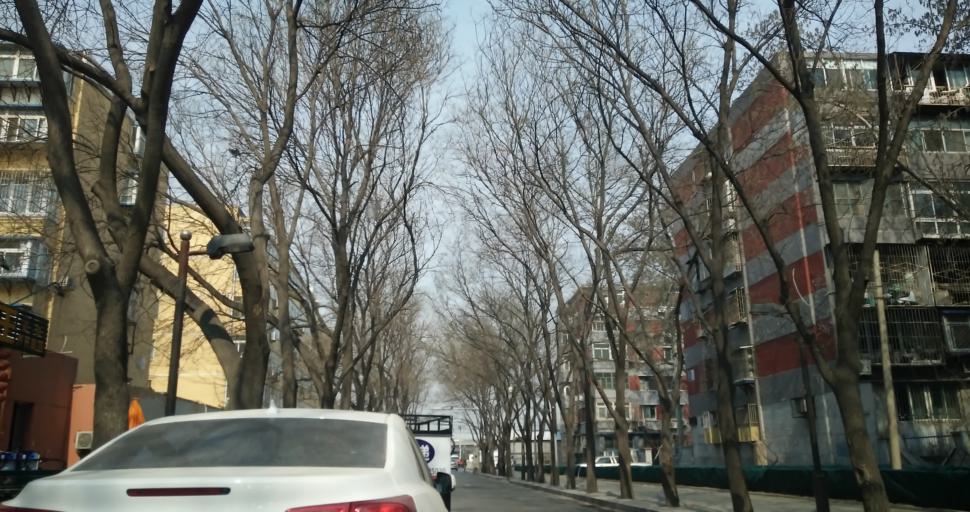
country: CN
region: Beijing
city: Dongfeng
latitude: 39.8672
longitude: 116.5043
